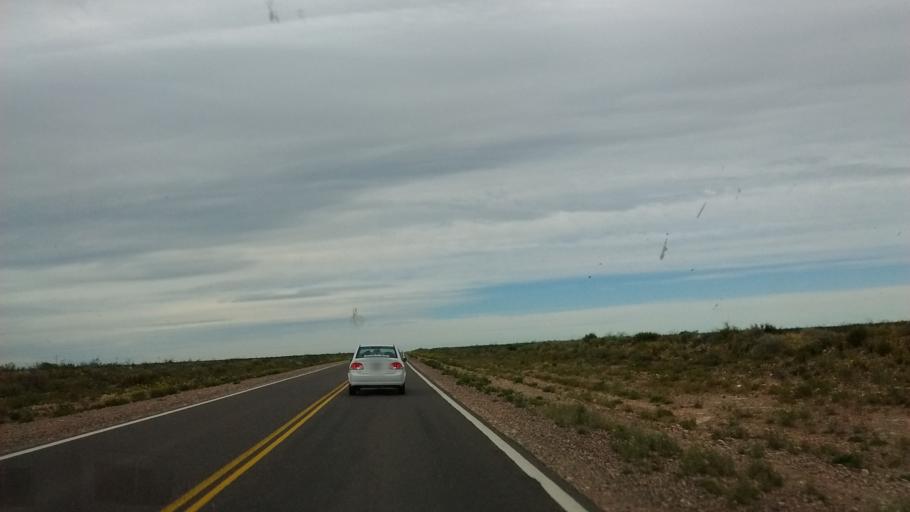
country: AR
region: Rio Negro
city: Contraalmirante Cordero
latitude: -38.3392
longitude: -68.0108
